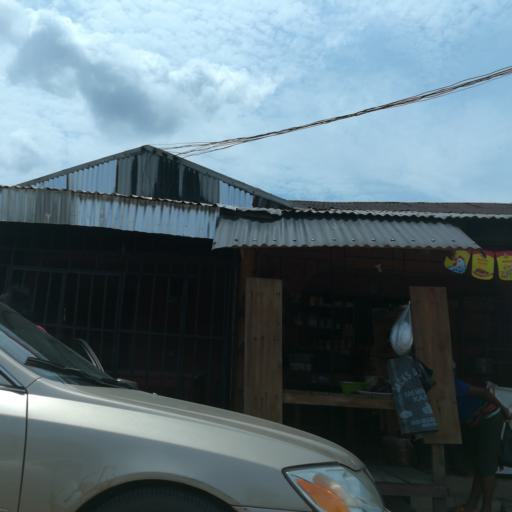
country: NG
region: Rivers
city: Port Harcourt
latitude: 4.7801
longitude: 7.0402
